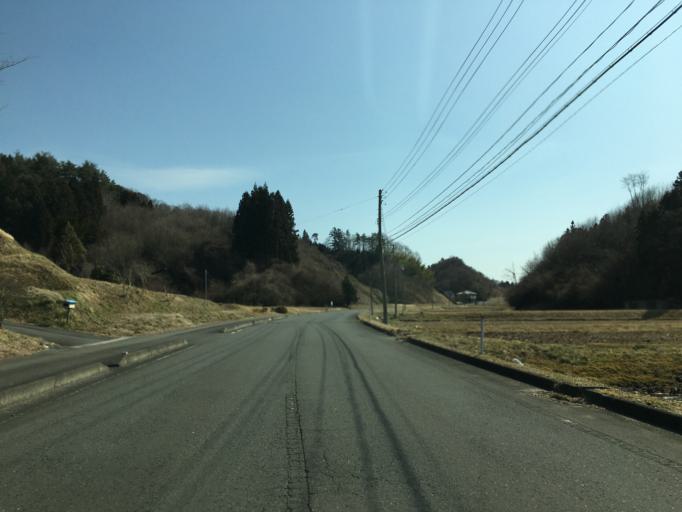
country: JP
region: Fukushima
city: Ishikawa
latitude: 37.0440
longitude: 140.4689
